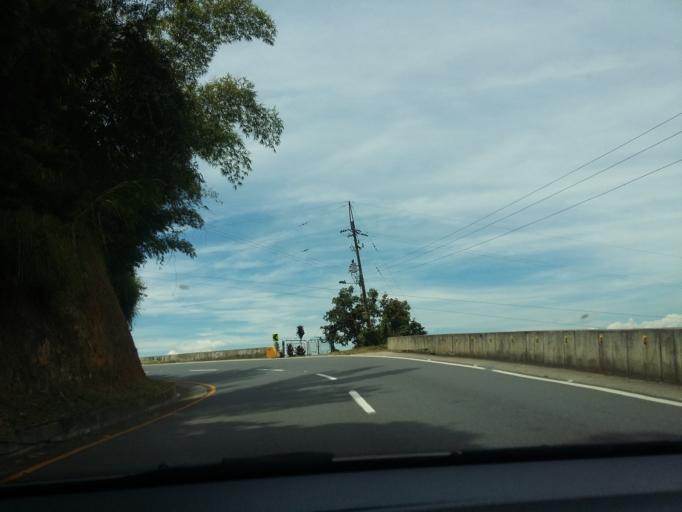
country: CO
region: Santander
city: Bucaramanga
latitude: 7.1100
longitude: -73.0795
